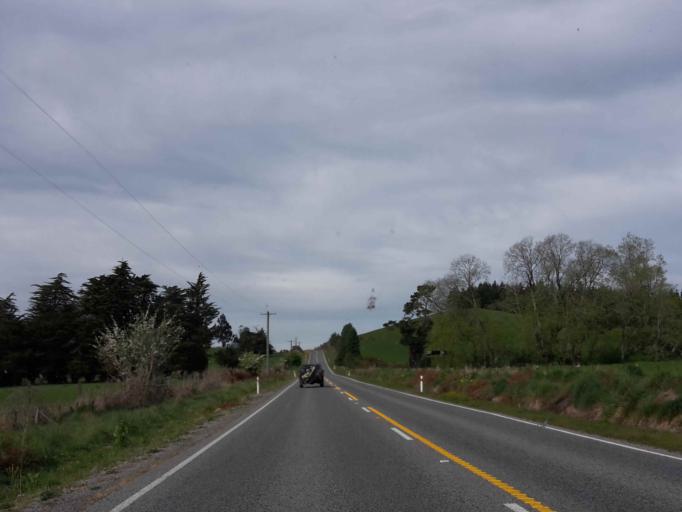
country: NZ
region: Canterbury
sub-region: Timaru District
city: Pleasant Point
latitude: -44.1265
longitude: 171.0960
